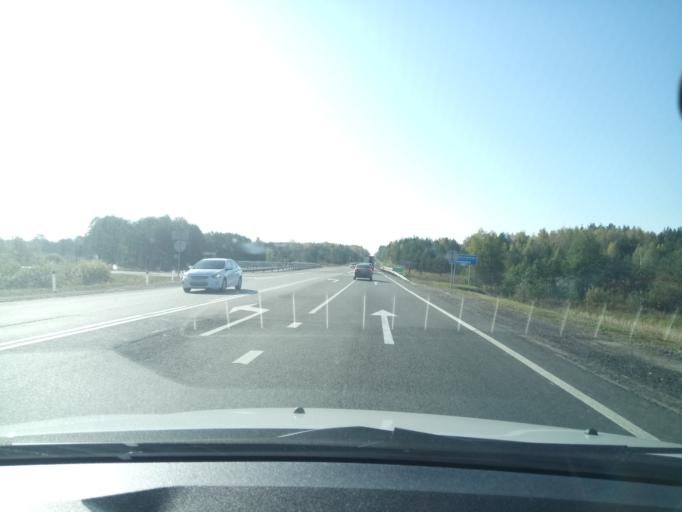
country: RU
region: Nizjnij Novgorod
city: Dal'neye Konstantinovo
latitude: 55.9607
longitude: 43.9756
